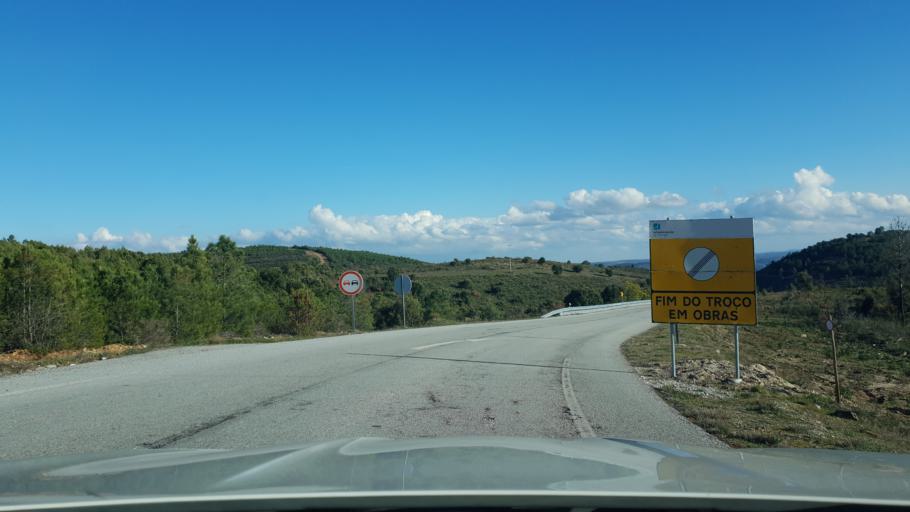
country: PT
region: Braganca
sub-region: Freixo de Espada A Cinta
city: Freixo de Espada a Cinta
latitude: 41.1279
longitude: -6.8164
